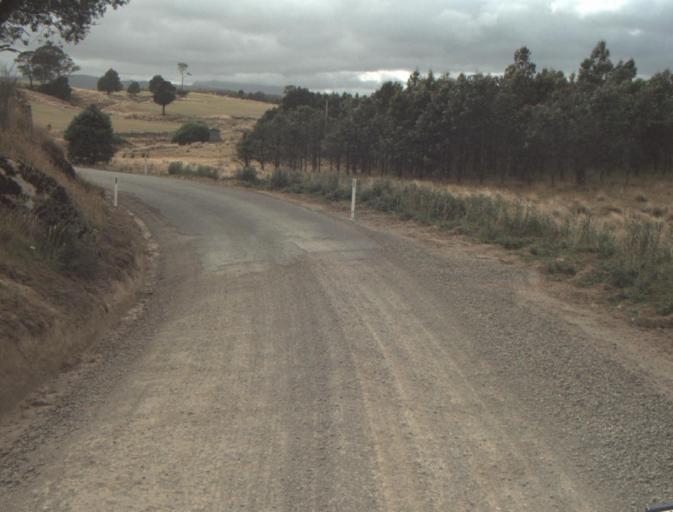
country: AU
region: Tasmania
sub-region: Dorset
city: Scottsdale
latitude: -41.3529
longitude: 147.4520
